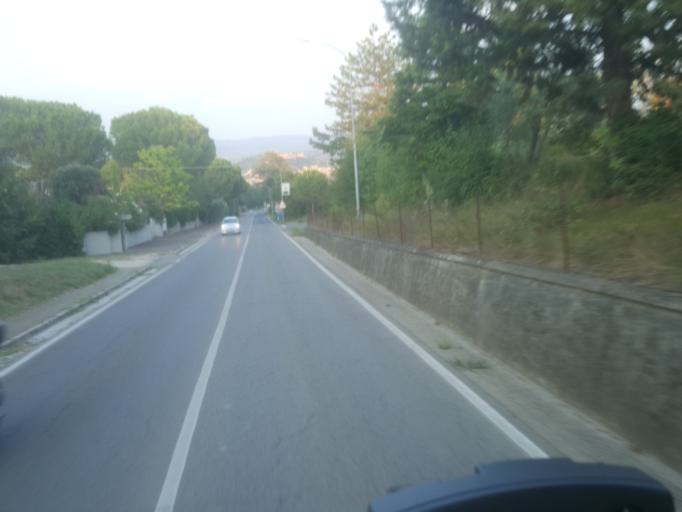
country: IT
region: Tuscany
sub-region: Province of Florence
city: Certaldo
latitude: 43.5445
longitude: 11.0168
